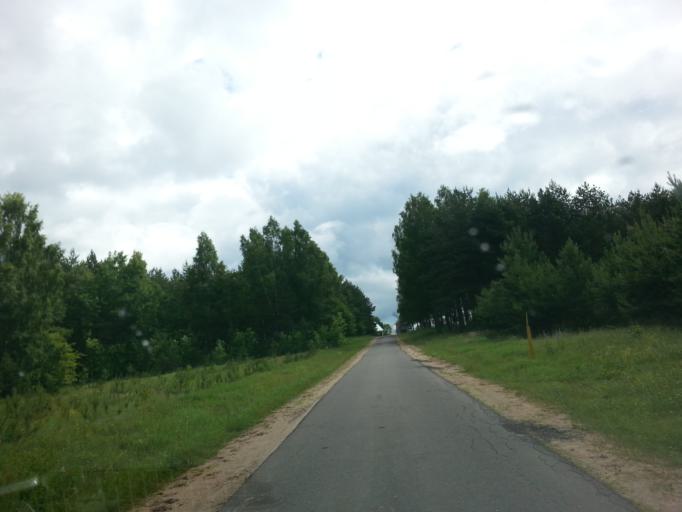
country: BY
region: Minsk
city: Narach
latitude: 54.8619
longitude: 26.7076
